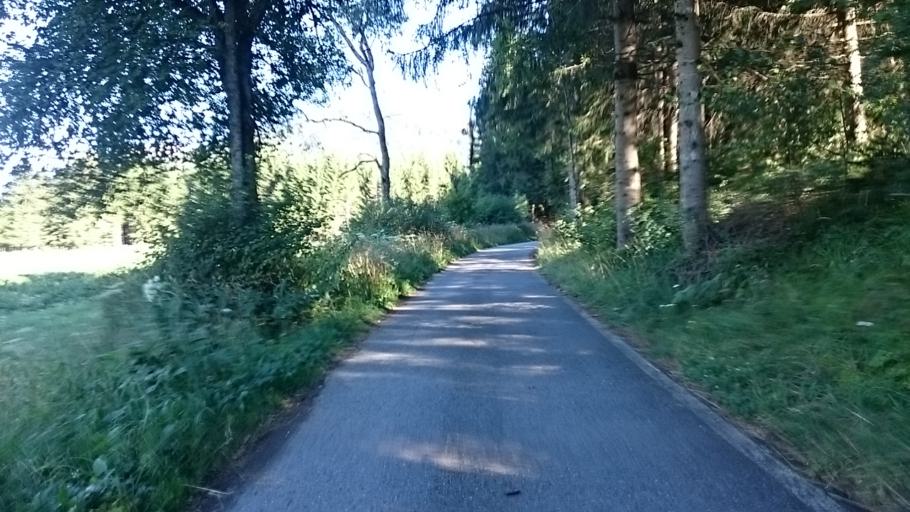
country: IT
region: Trentino-Alto Adige
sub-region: Bolzano
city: Braies
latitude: 46.7414
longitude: 12.1281
